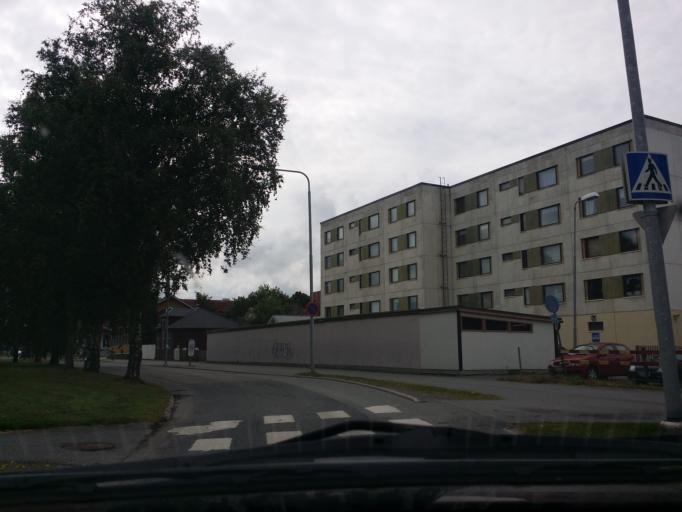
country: FI
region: Satakunta
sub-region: Pori
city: Pori
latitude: 61.4971
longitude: 21.8031
